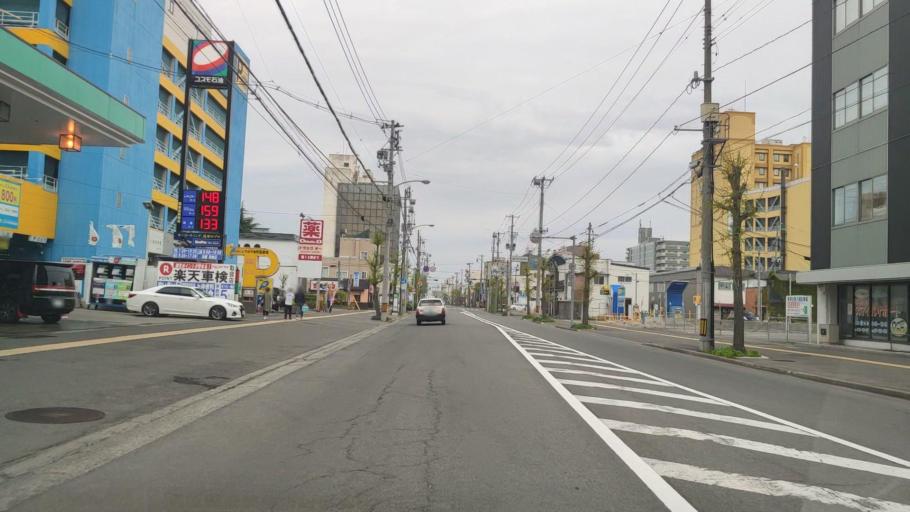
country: JP
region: Aomori
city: Aomori Shi
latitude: 40.8241
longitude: 140.7504
